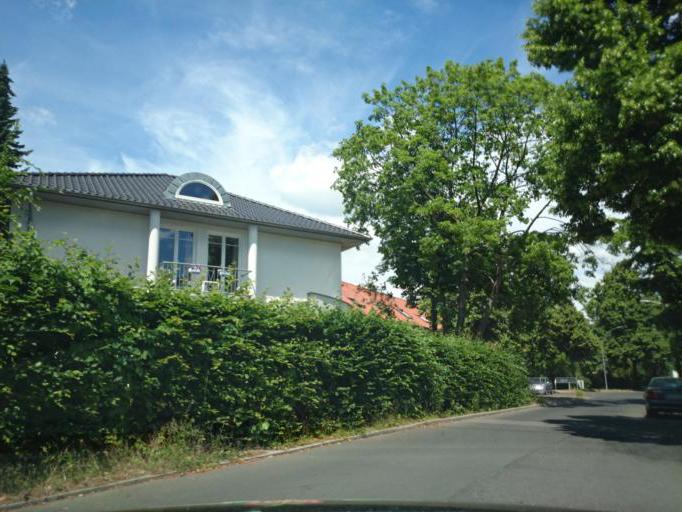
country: DE
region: Berlin
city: Lichterfelde
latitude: 52.4184
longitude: 13.3275
